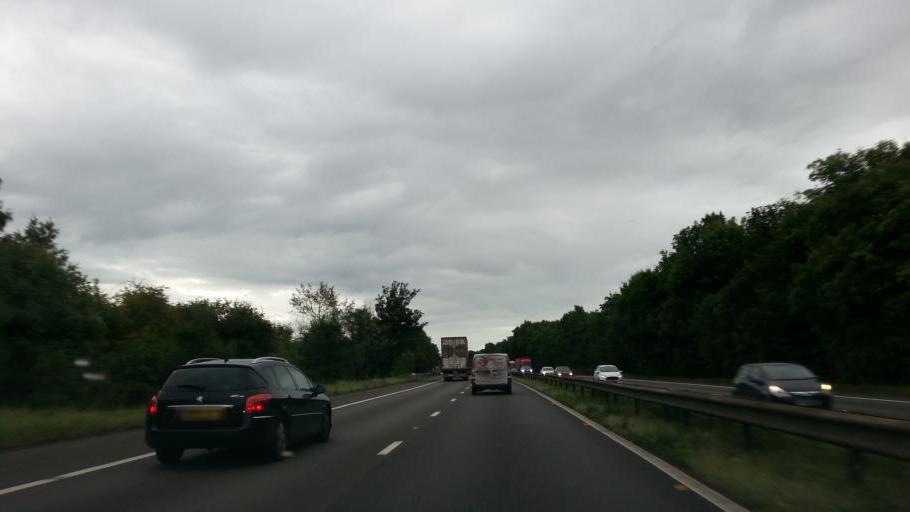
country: GB
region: England
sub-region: Doncaster
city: Marr
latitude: 53.5563
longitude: -1.2161
